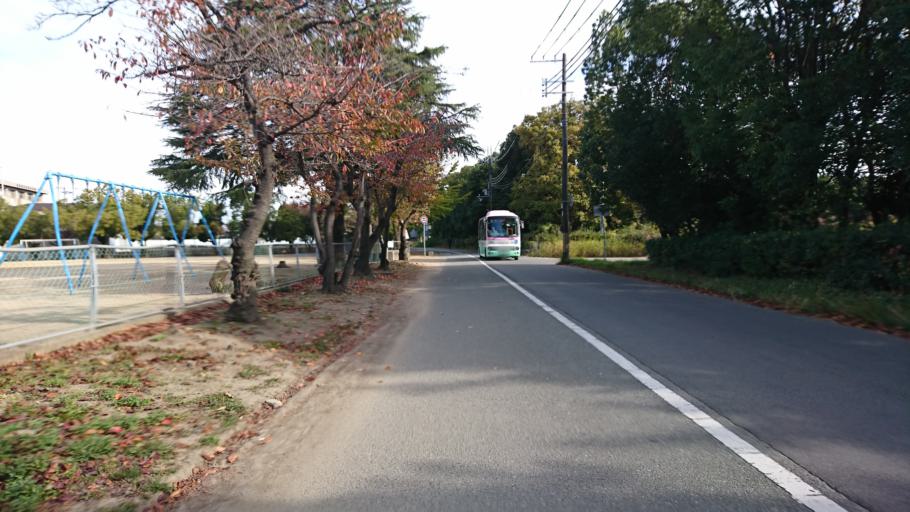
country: JP
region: Hyogo
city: Kakogawacho-honmachi
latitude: 34.7440
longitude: 134.7991
